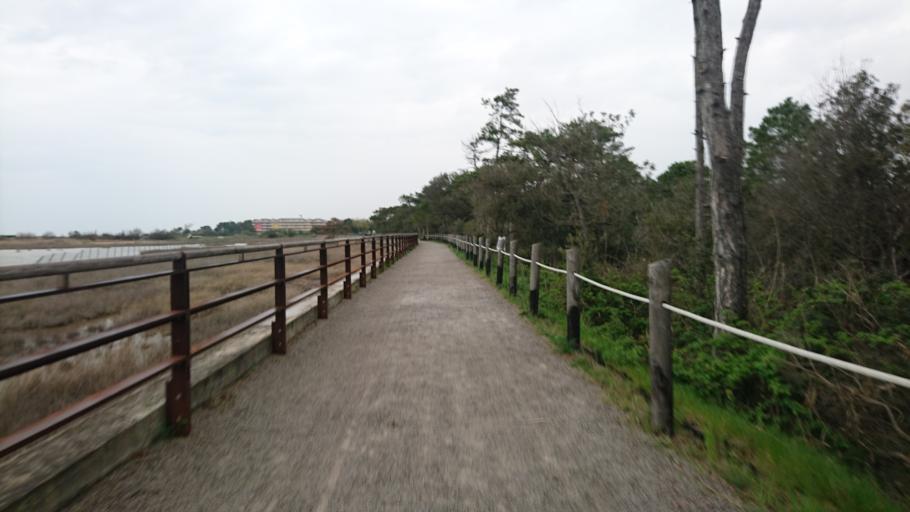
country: IT
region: Veneto
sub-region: Provincia di Venezia
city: Bibione
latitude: 45.6357
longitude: 13.0802
